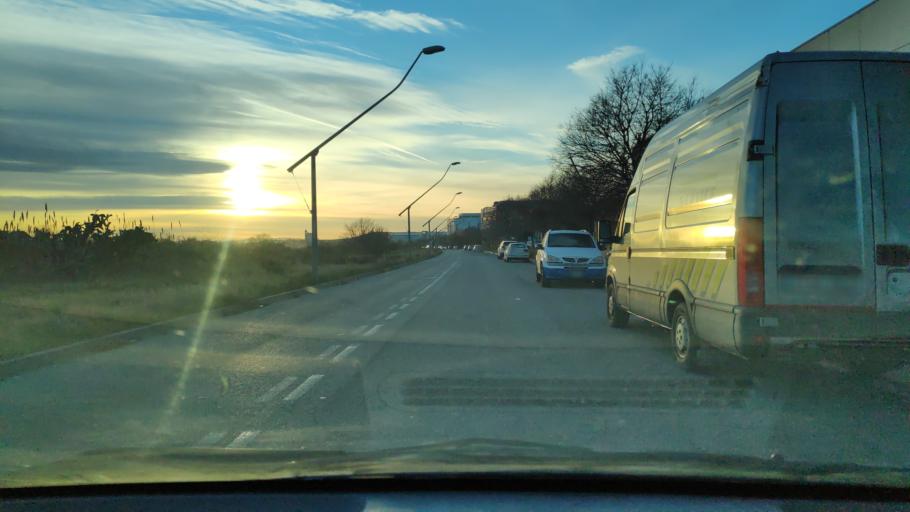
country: ES
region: Catalonia
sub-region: Provincia de Barcelona
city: Montmelo
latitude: 41.5463
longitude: 2.2422
